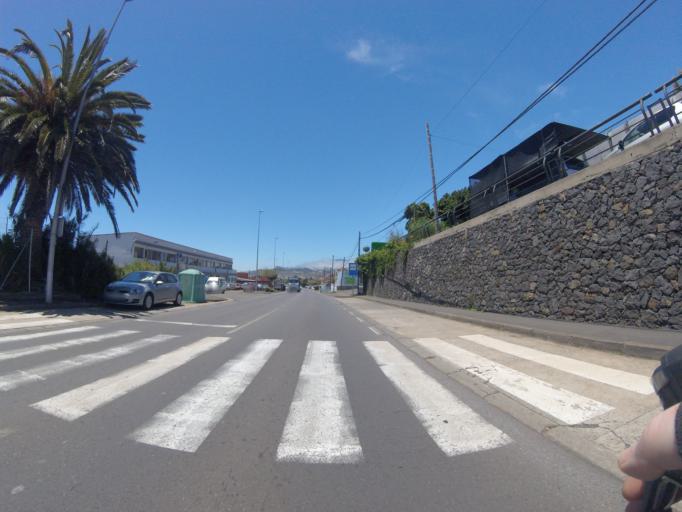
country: ES
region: Canary Islands
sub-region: Provincia de Santa Cruz de Tenerife
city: Tegueste
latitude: 28.5083
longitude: -16.3099
